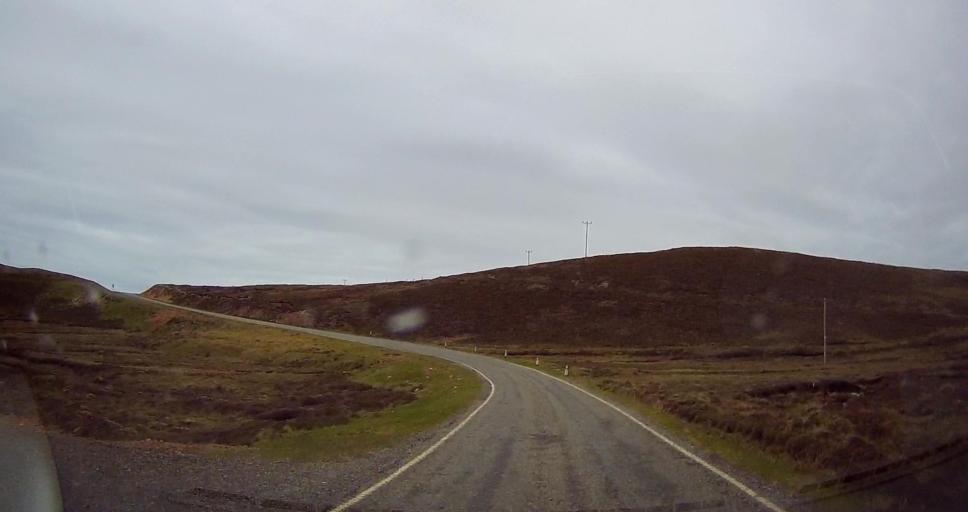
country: GB
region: Scotland
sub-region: Shetland Islands
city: Lerwick
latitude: 60.4867
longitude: -1.5237
